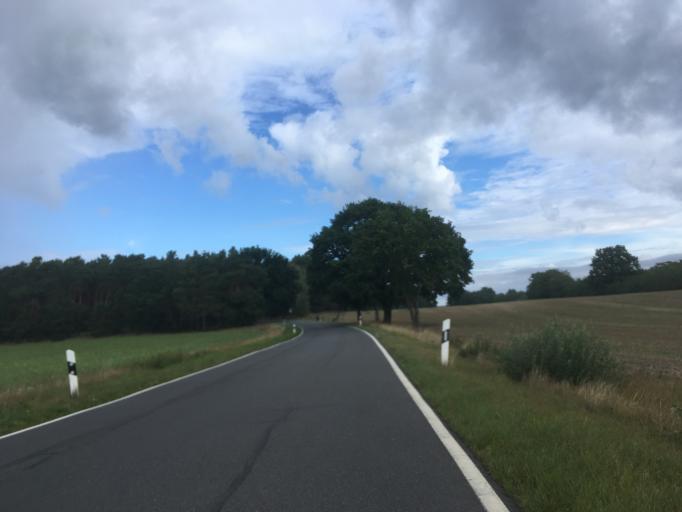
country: DE
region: Brandenburg
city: Halbe
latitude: 52.0613
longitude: 13.7226
